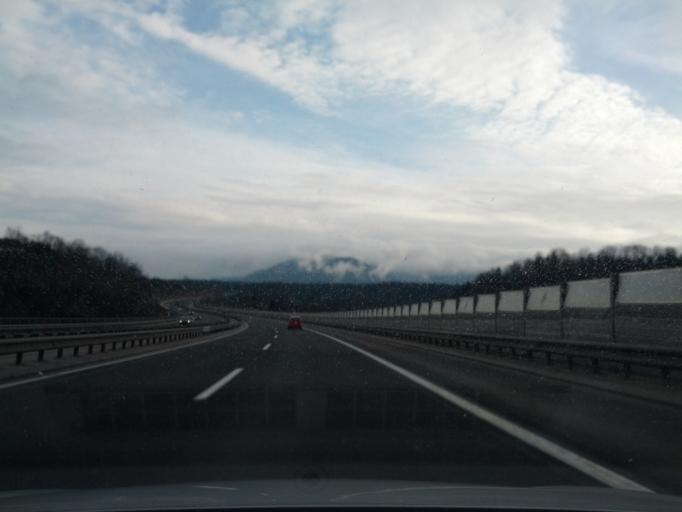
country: SI
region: Naklo
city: Naklo
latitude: 46.2937
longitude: 14.2844
